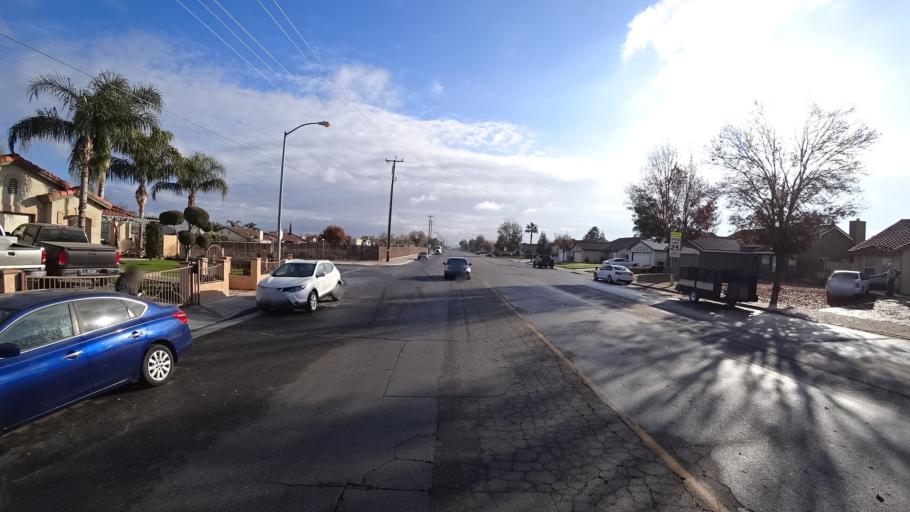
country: US
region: California
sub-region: Kern County
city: Greenfield
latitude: 35.2886
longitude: -119.0091
